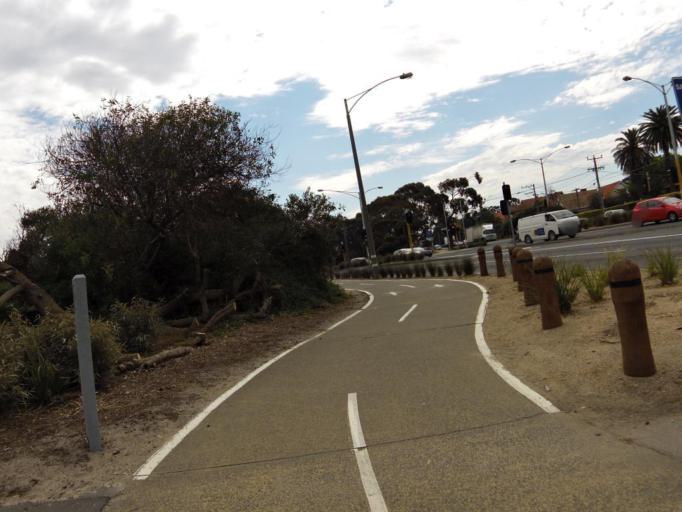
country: AU
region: Victoria
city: Hampton
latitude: -37.9441
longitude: 145.0011
